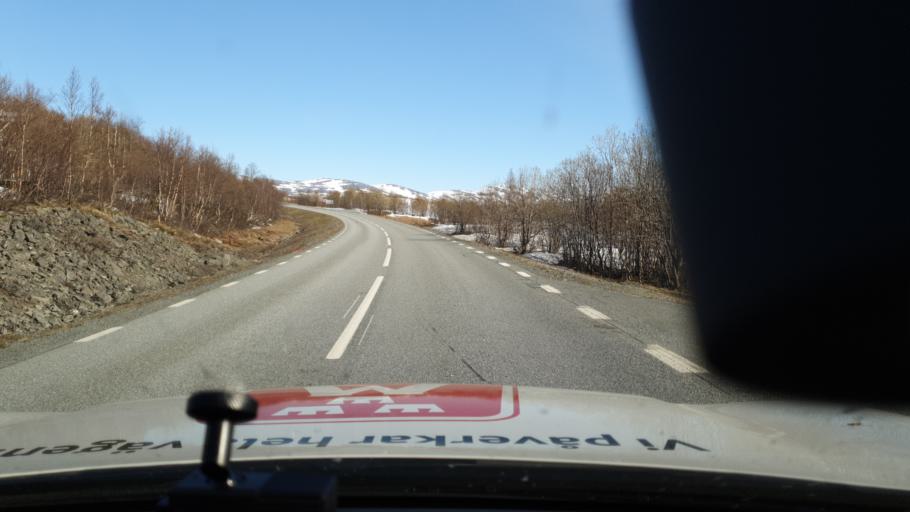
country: NO
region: Nordland
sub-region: Rana
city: Mo i Rana
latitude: 66.1276
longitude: 14.6023
